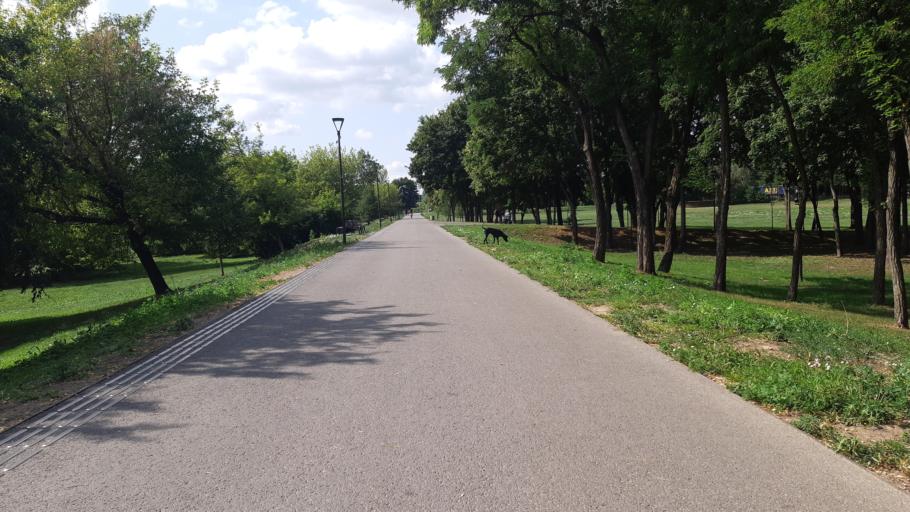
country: LT
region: Kauno apskritis
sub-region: Kaunas
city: Kaunas
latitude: 54.8965
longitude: 23.8805
